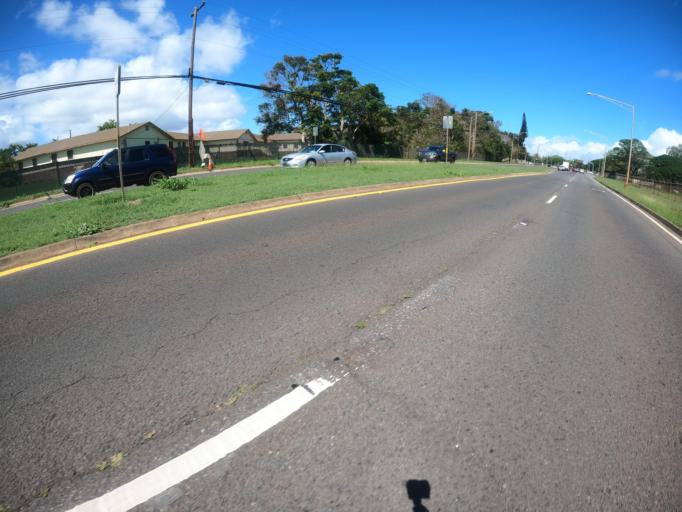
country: US
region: Hawaii
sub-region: Honolulu County
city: Schofield Barracks
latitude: 21.4812
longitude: -158.0487
